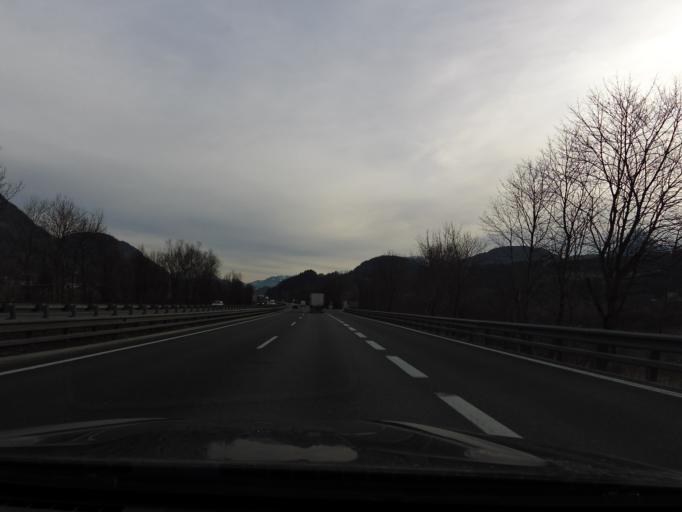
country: AT
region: Tyrol
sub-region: Politischer Bezirk Kufstein
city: Langkampfen
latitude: 47.5397
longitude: 12.1115
